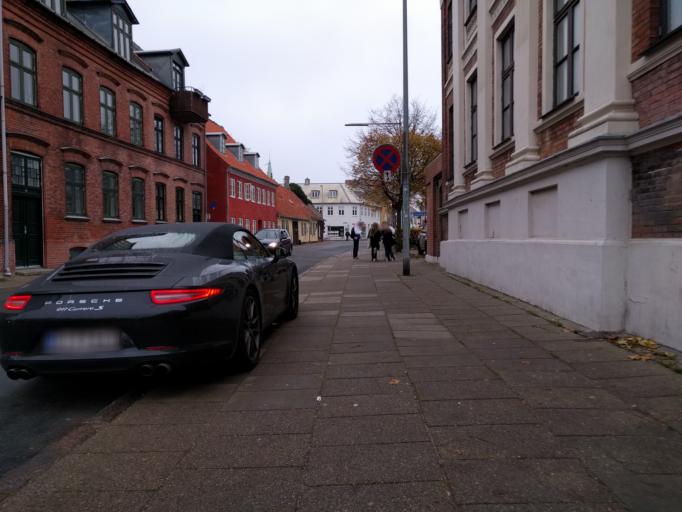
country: DK
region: Capital Region
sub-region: Helsingor Kommune
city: Helsingor
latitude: 56.0381
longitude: 12.6091
